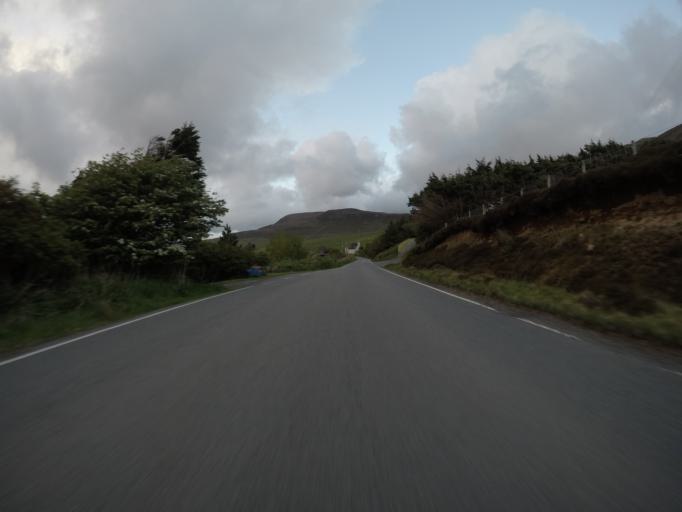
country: GB
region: Scotland
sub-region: Highland
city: Portree
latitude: 57.6115
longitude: -6.3725
